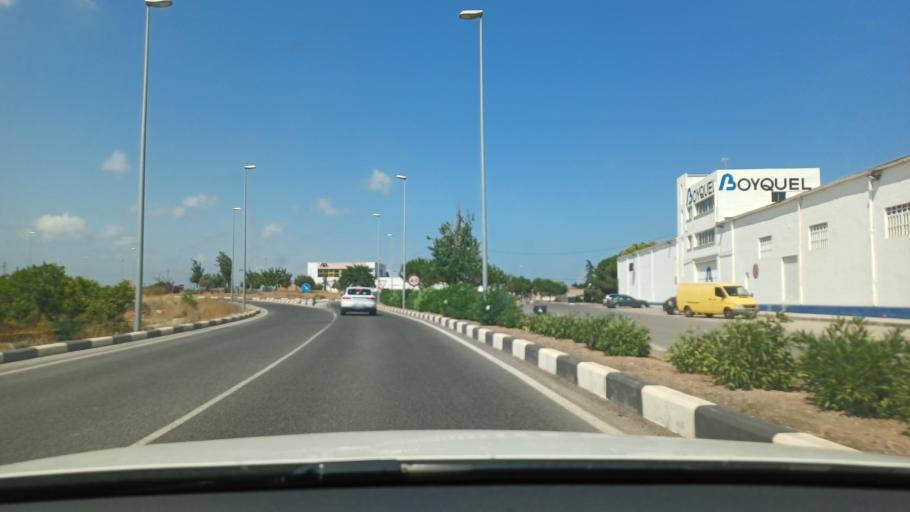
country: ES
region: Valencia
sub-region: Provincia de Castello
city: Chilches
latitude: 39.7808
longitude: -0.1938
